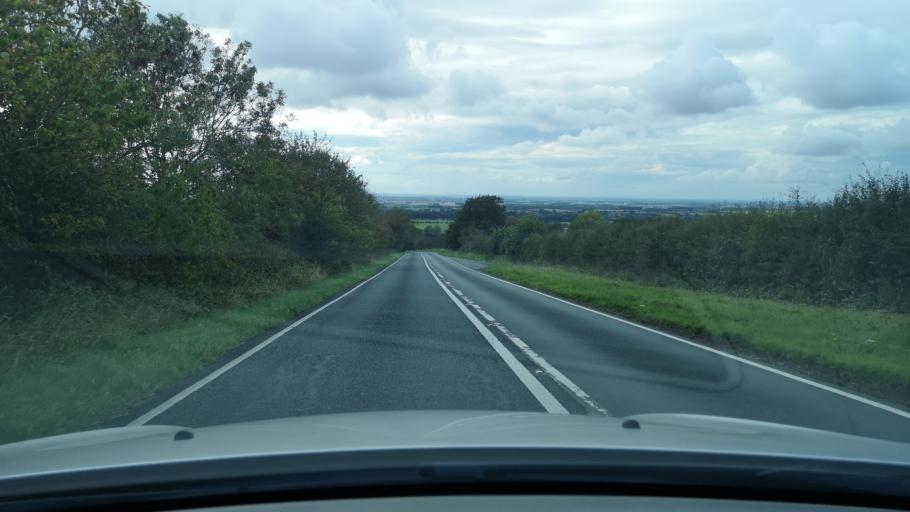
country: GB
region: England
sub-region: East Riding of Yorkshire
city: South Cave
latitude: 53.7959
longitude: -0.6020
